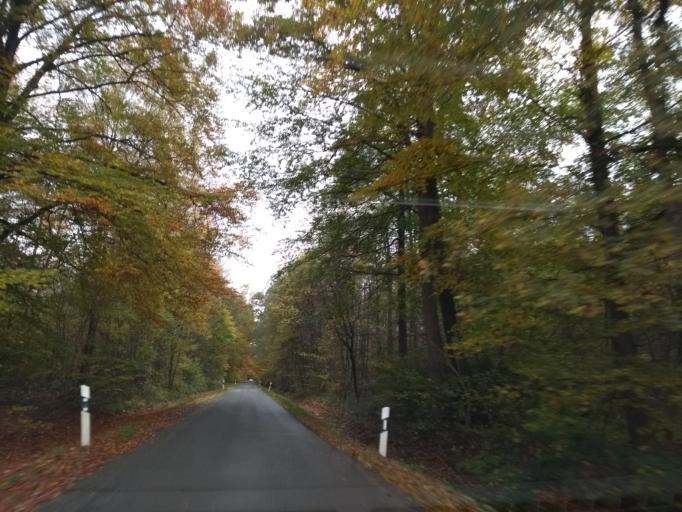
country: DE
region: North Rhine-Westphalia
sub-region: Regierungsbezirk Detmold
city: Hovelhof
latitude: 51.7832
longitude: 8.6956
